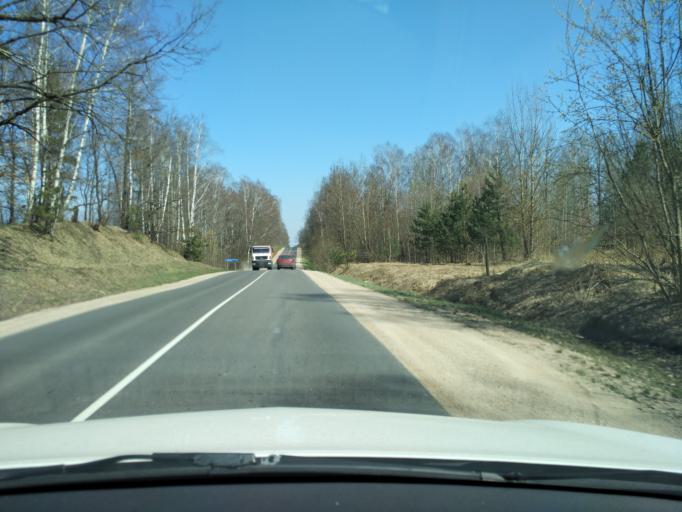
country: BY
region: Minsk
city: Slabada
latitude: 53.9910
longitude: 27.9652
